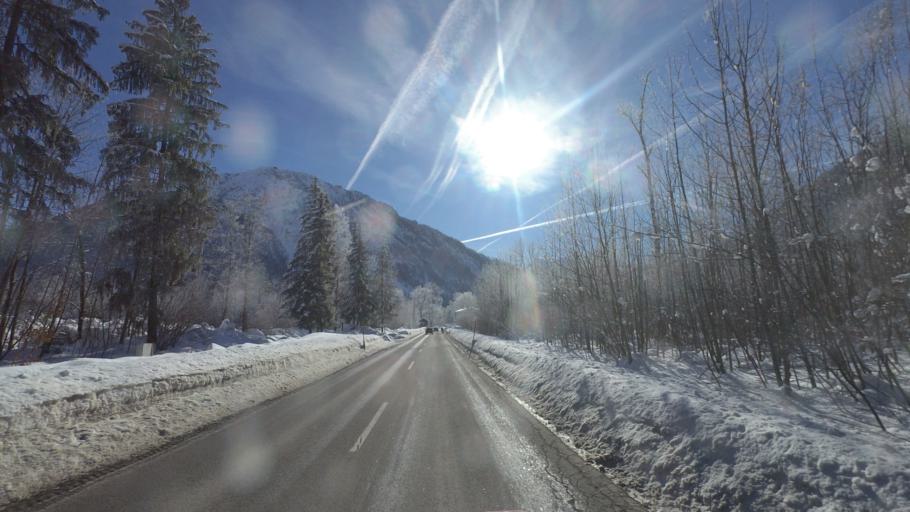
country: DE
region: Bavaria
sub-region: Upper Bavaria
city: Ruhpolding
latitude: 47.7467
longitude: 12.6555
